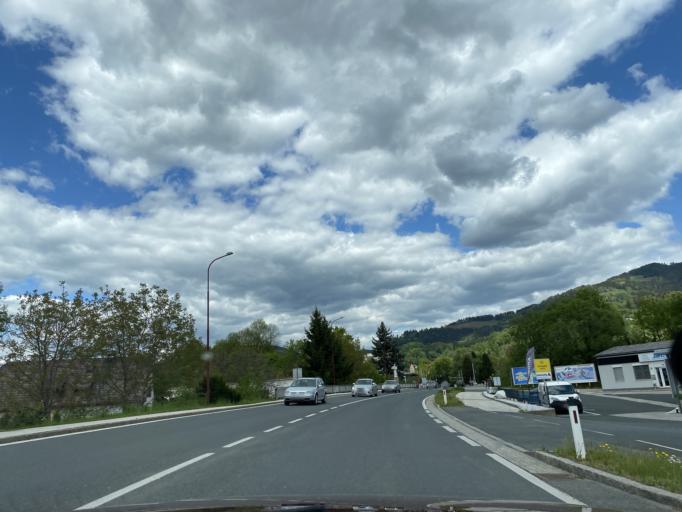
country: AT
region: Carinthia
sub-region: Politischer Bezirk Wolfsberg
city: Wolfsberg
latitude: 46.8293
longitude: 14.8397
